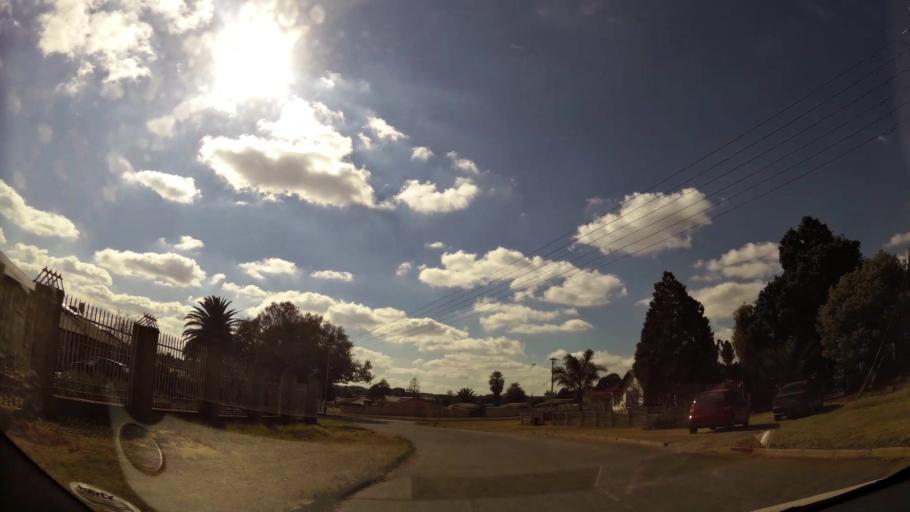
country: ZA
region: Gauteng
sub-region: West Rand District Municipality
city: Krugersdorp
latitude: -26.1224
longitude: 27.8060
